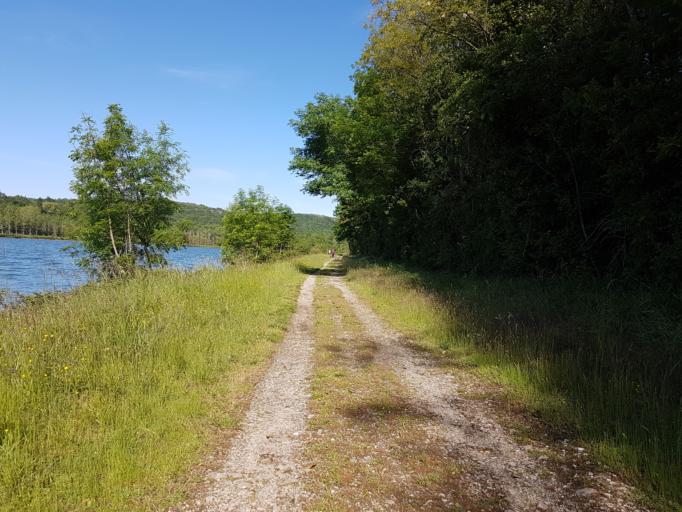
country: FR
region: Rhone-Alpes
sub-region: Departement de l'Ain
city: Villebois
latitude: 45.8389
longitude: 5.4238
